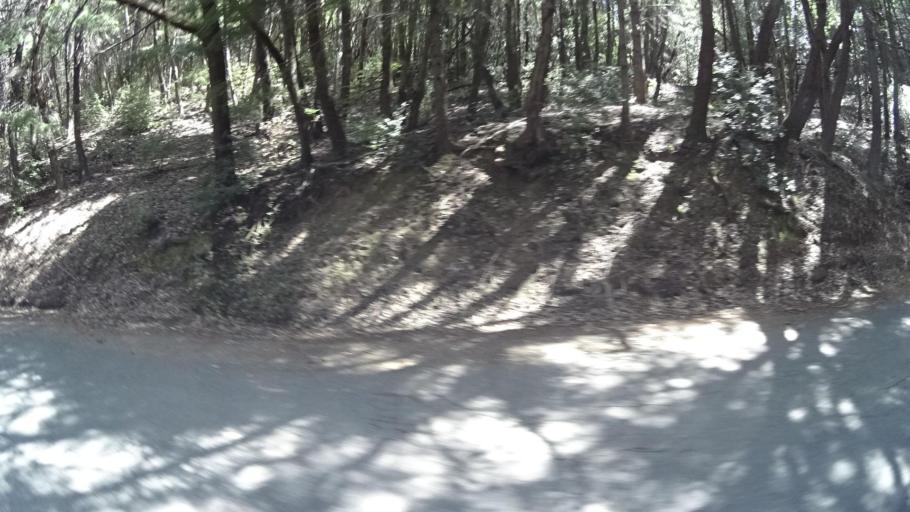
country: US
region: California
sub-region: Humboldt County
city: Redway
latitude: 40.1049
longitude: -123.9534
